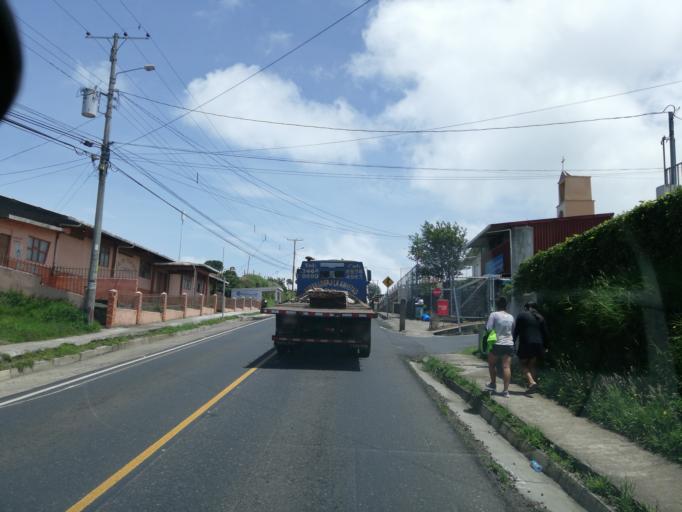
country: CR
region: Alajuela
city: Zarcero
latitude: 10.2176
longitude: -84.4016
